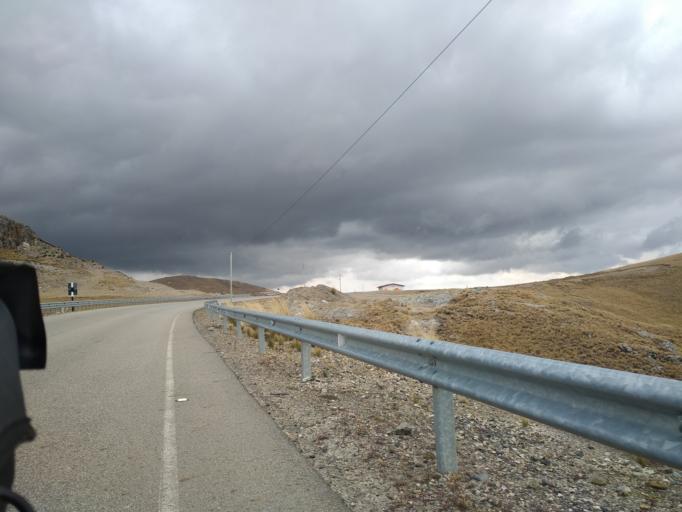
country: PE
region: La Libertad
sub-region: Provincia de Santiago de Chuco
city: Quiruvilca
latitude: -7.9902
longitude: -78.2858
